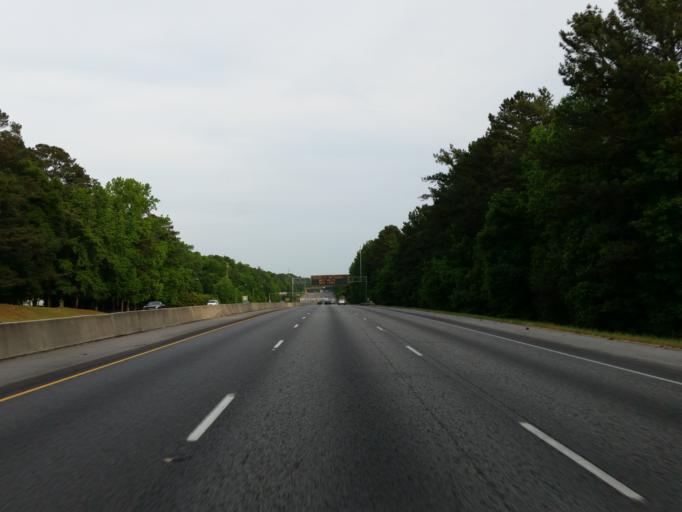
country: US
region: Georgia
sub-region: Bibb County
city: West Point
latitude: 32.8671
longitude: -83.7551
